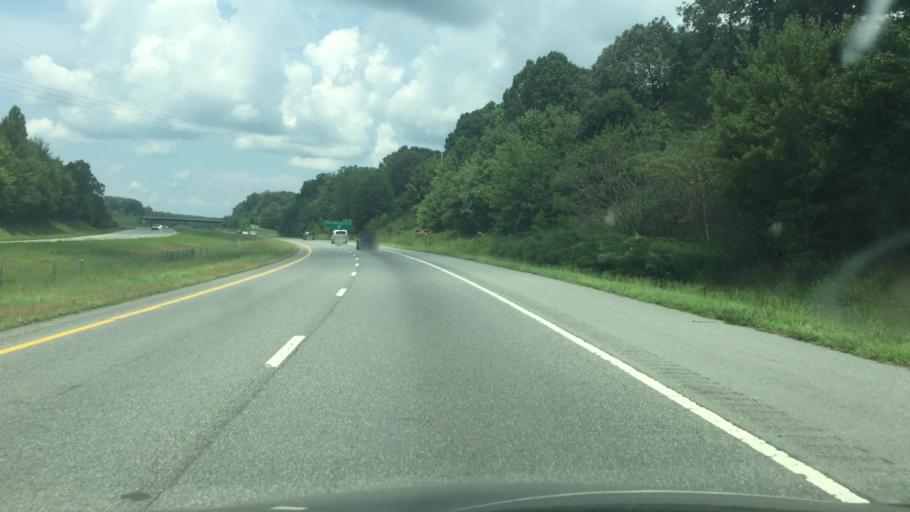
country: US
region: North Carolina
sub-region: Randolph County
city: Asheboro
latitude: 35.5871
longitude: -79.8085
